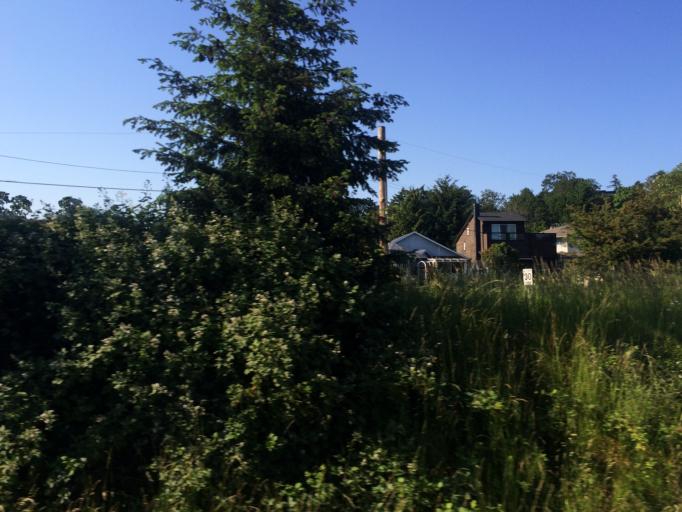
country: CA
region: British Columbia
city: Victoria
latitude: 48.4641
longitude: -123.4248
